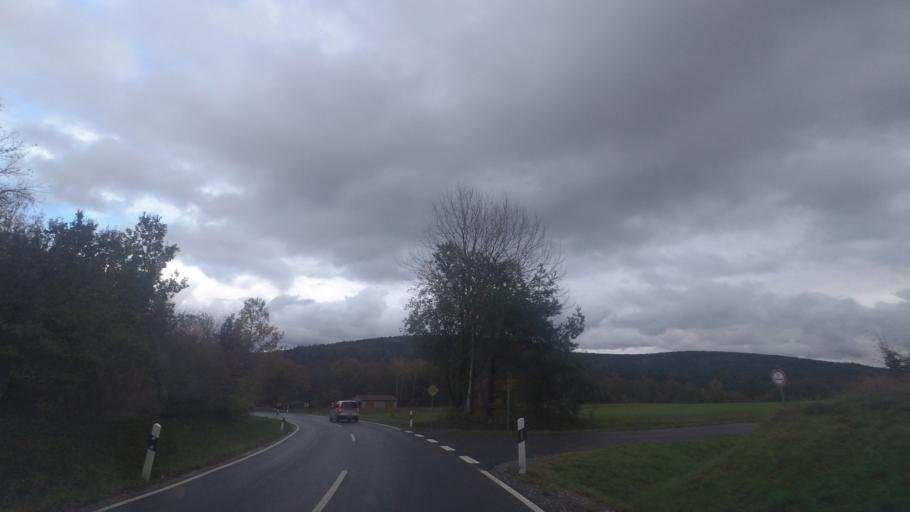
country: DE
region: Bavaria
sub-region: Regierungsbezirk Unterfranken
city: Oberelsbach
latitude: 50.3757
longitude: 10.1065
